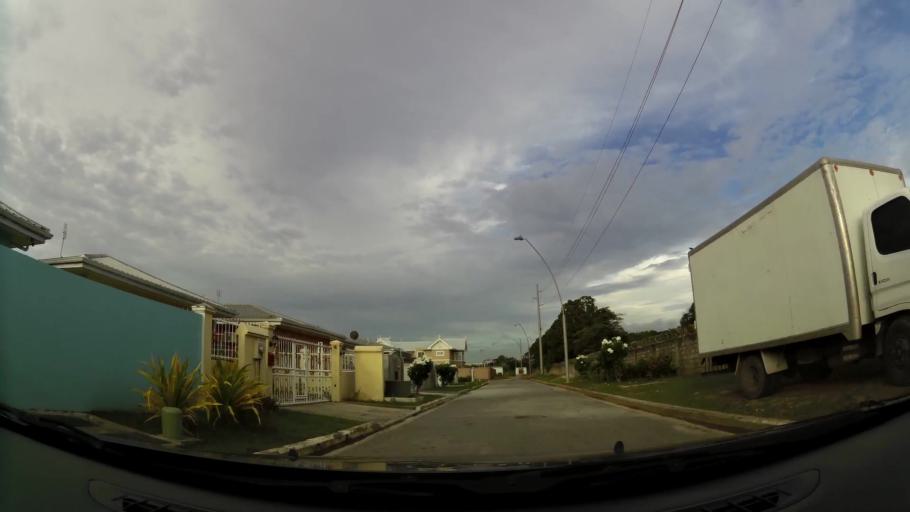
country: TT
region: Tunapuna/Piarco
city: Tunapuna
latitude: 10.6417
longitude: -61.4119
